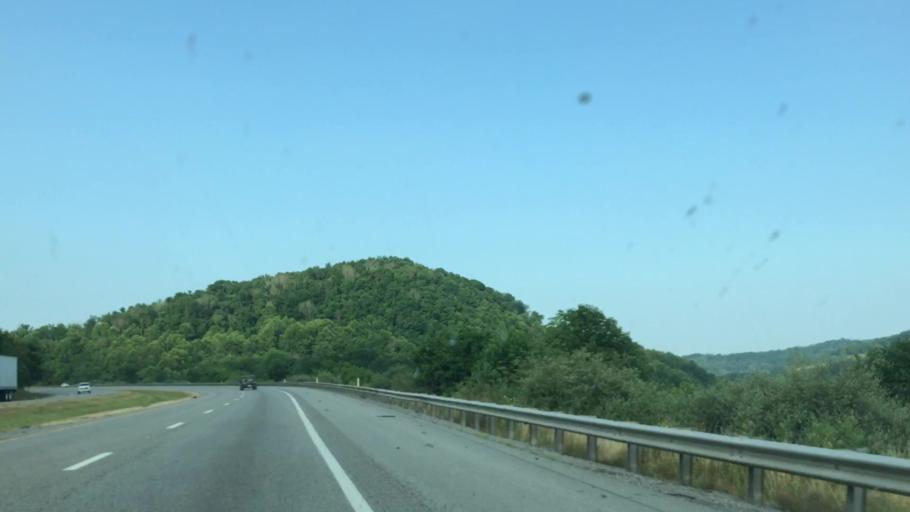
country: US
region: West Virginia
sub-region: Lewis County
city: Weston
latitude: 39.0457
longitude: -80.4124
